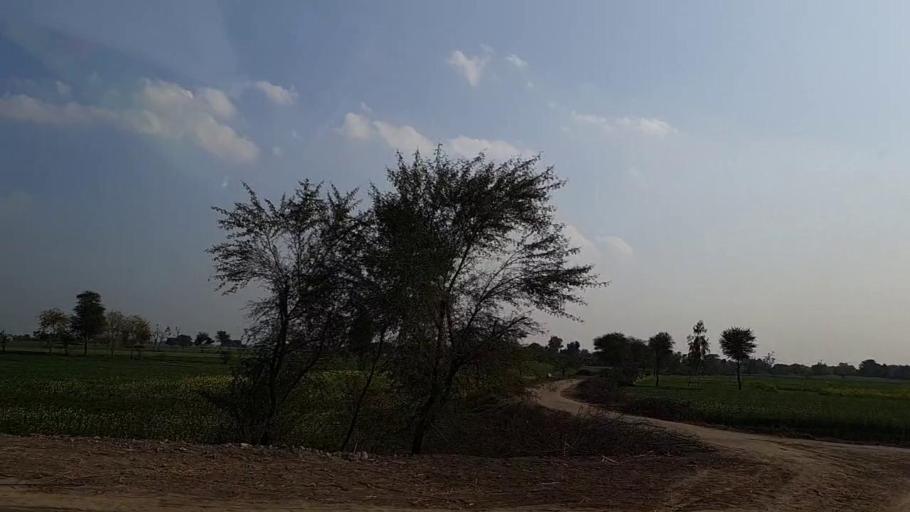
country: PK
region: Sindh
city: Nawabshah
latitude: 26.1487
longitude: 68.3901
